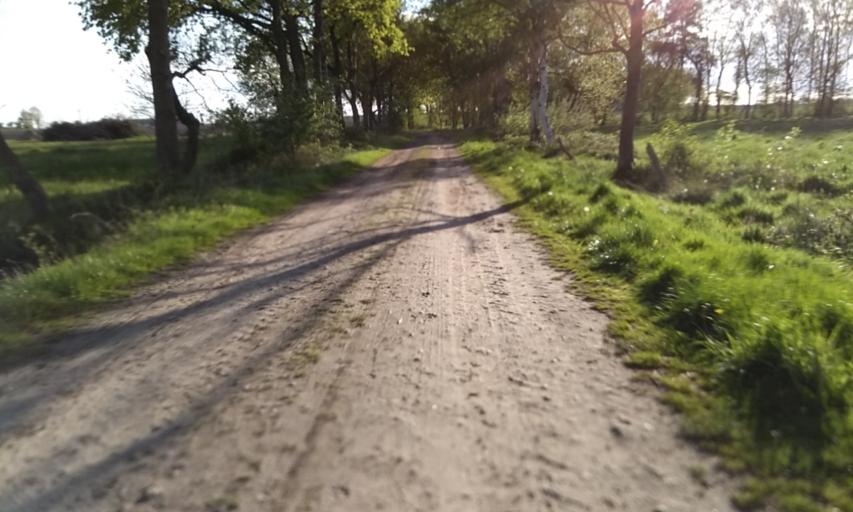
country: DE
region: Lower Saxony
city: Beckdorf
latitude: 53.4067
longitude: 9.6016
